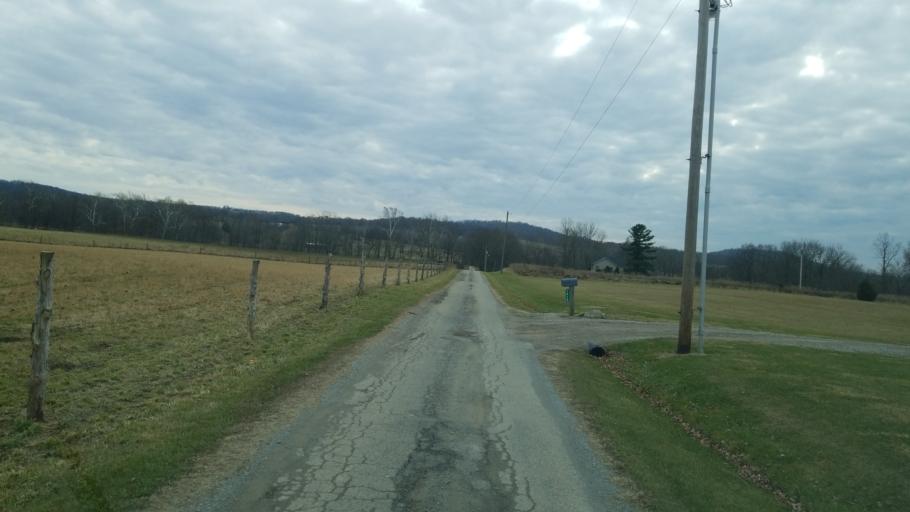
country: US
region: Ohio
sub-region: Highland County
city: Greenfield
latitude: 39.3274
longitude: -83.3265
